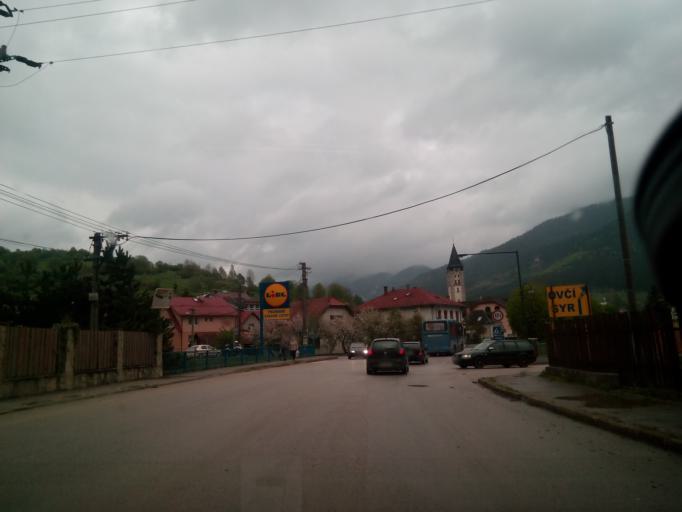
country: SK
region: Zilinsky
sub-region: Okres Zilina
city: Terchova
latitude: 49.2590
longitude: 19.0281
